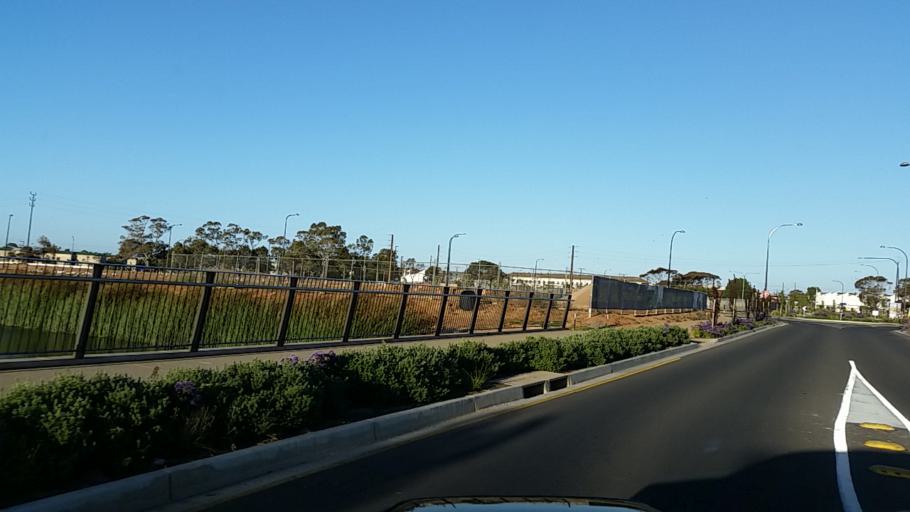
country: AU
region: South Australia
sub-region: Charles Sturt
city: Woodville North
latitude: -34.8684
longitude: 138.5323
